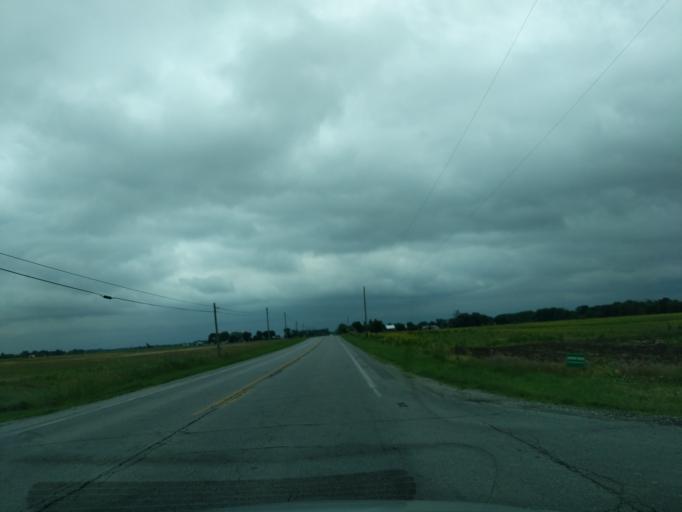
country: US
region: Indiana
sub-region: Madison County
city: Frankton
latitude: 40.2774
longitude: -85.7662
